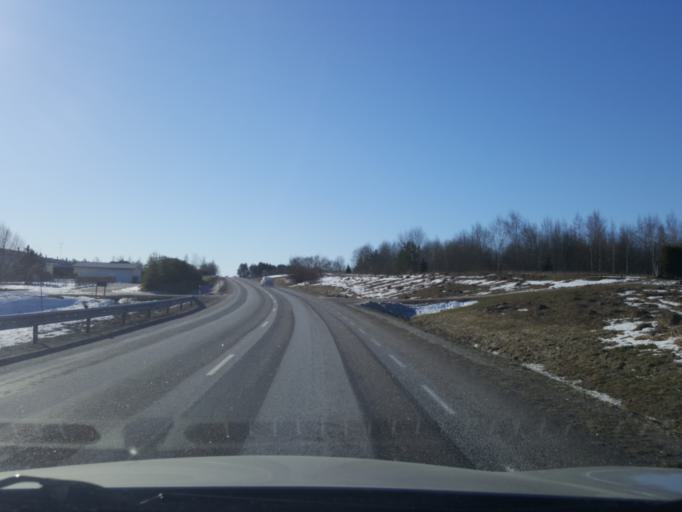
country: EE
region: Viljandimaa
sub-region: Viljandi linn
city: Viljandi
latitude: 58.3840
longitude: 25.6063
